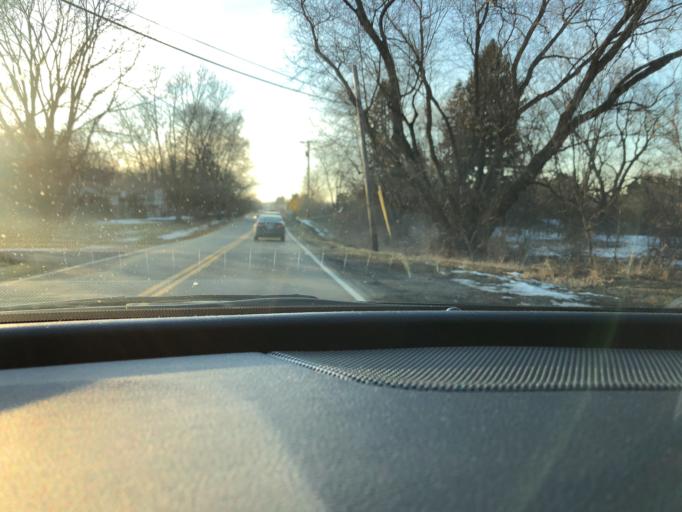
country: US
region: Ohio
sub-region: Stark County
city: Perry Heights
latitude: 40.8120
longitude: -81.4544
